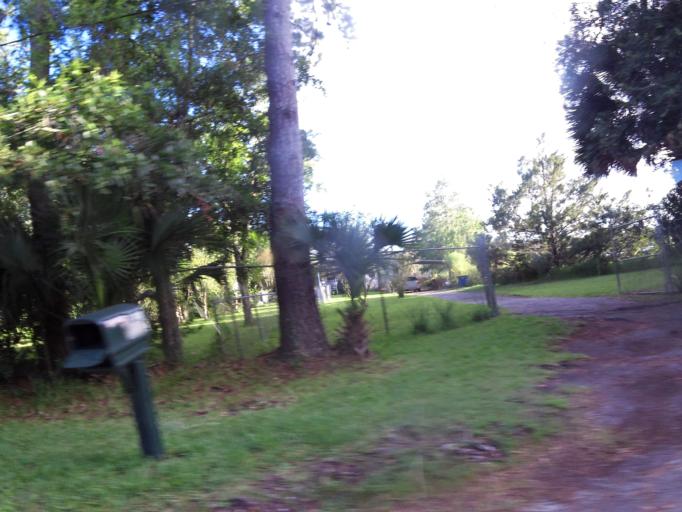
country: US
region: Florida
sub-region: Duval County
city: Jacksonville
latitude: 30.4208
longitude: -81.6985
